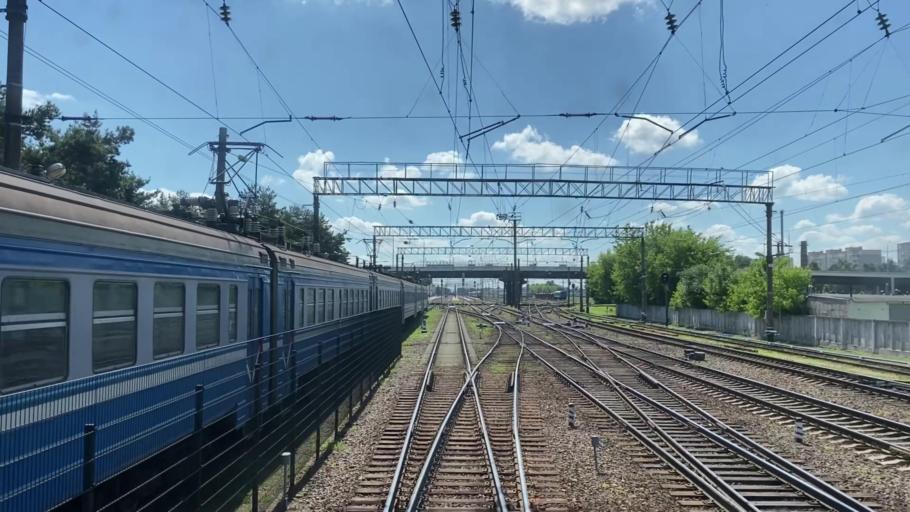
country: BY
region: Brest
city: Baranovichi
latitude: 53.1338
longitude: 26.0373
